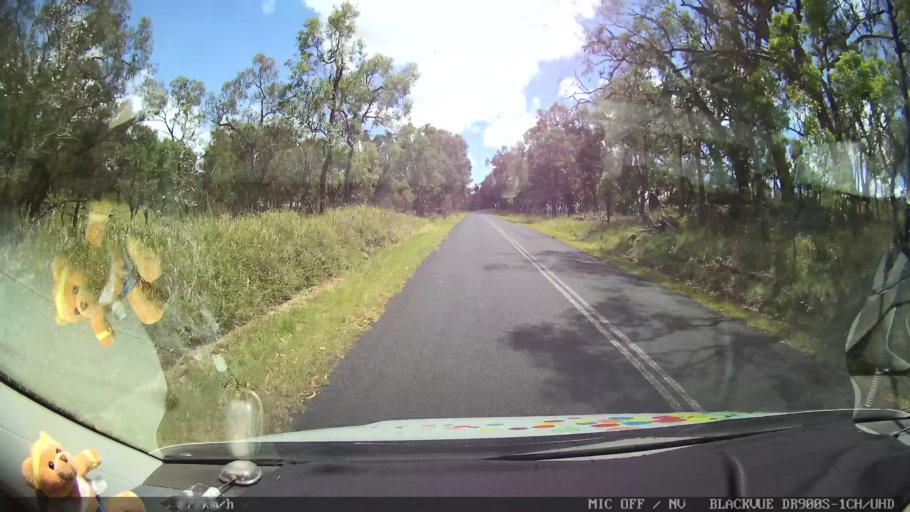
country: AU
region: New South Wales
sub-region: Glen Innes Severn
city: Glen Innes
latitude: -29.4889
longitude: 151.6829
